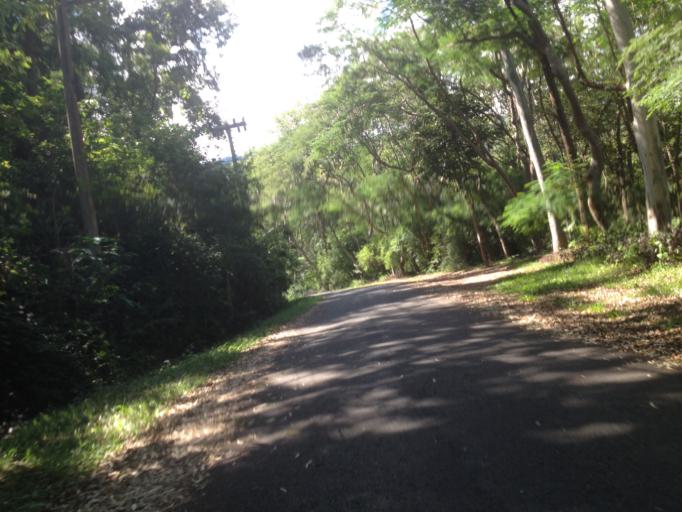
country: TH
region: Chiang Mai
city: Chiang Mai
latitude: 18.7914
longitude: 98.9456
